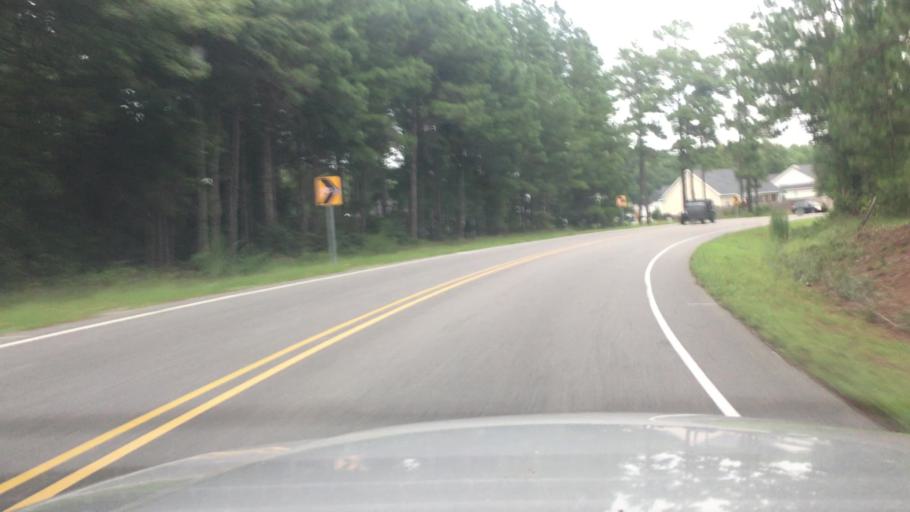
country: US
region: North Carolina
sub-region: Hoke County
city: Rockfish
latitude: 34.9892
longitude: -79.0277
